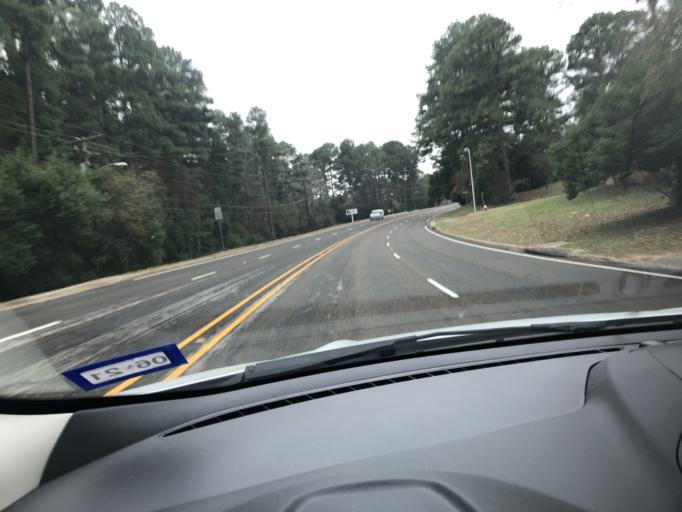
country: US
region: Texas
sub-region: Nacogdoches County
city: Nacogdoches
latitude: 31.6287
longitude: -94.6300
